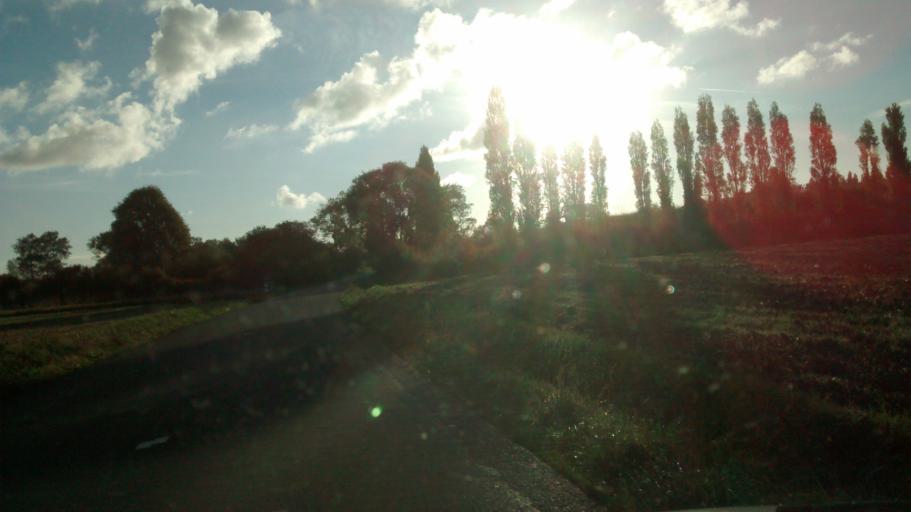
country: FR
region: Brittany
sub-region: Departement d'Ille-et-Vilaine
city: Saint-Meloir-des-Ondes
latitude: 48.6296
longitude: -1.8788
